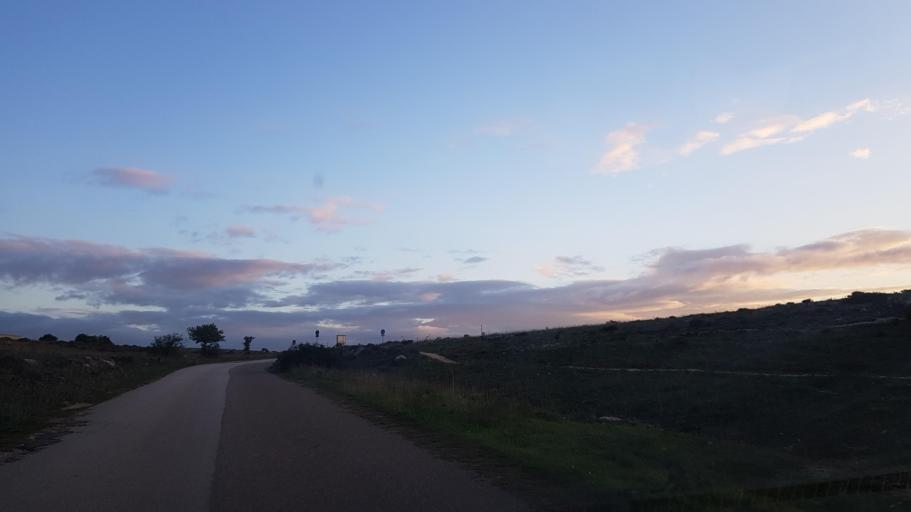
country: IT
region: Basilicate
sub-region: Provincia di Matera
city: Matera
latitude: 40.6739
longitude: 16.6277
